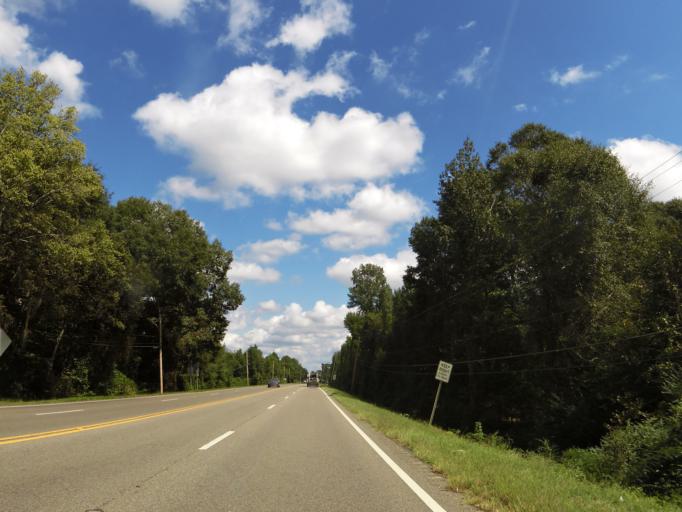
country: US
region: Alabama
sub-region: Dallas County
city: Selma
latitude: 32.3858
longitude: -87.0846
